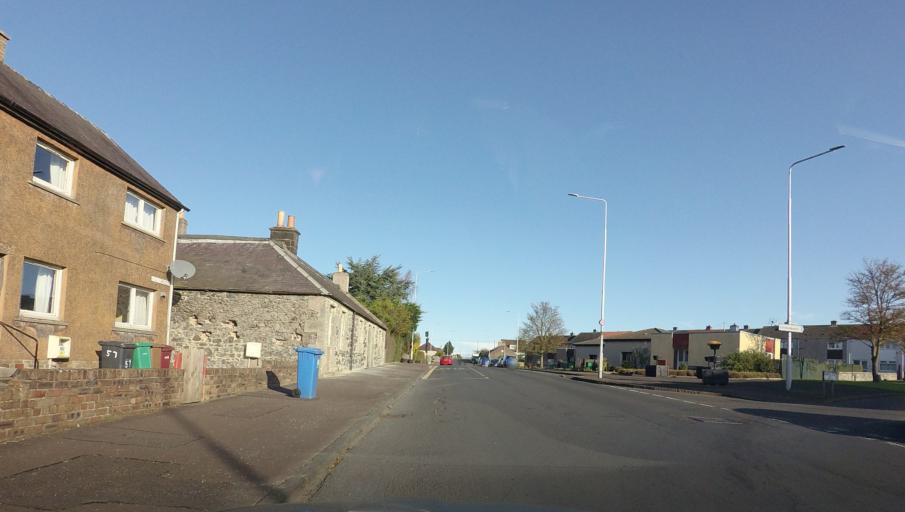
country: GB
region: Scotland
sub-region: Fife
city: Townhill
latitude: 56.0985
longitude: -3.4072
